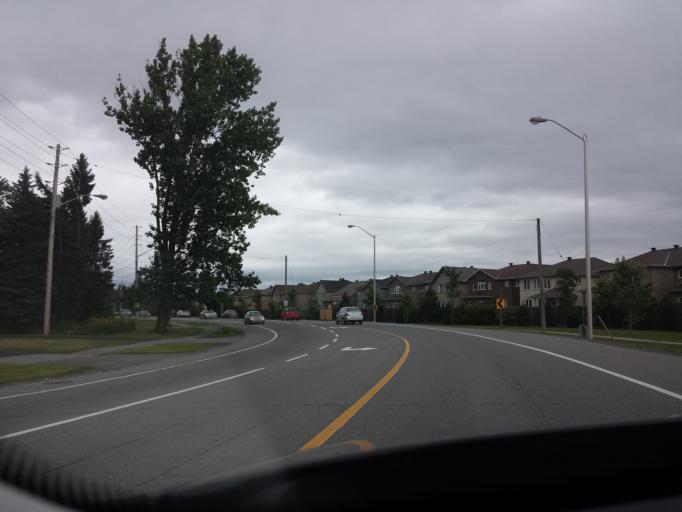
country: CA
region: Ontario
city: Ottawa
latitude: 45.3585
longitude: -75.7000
